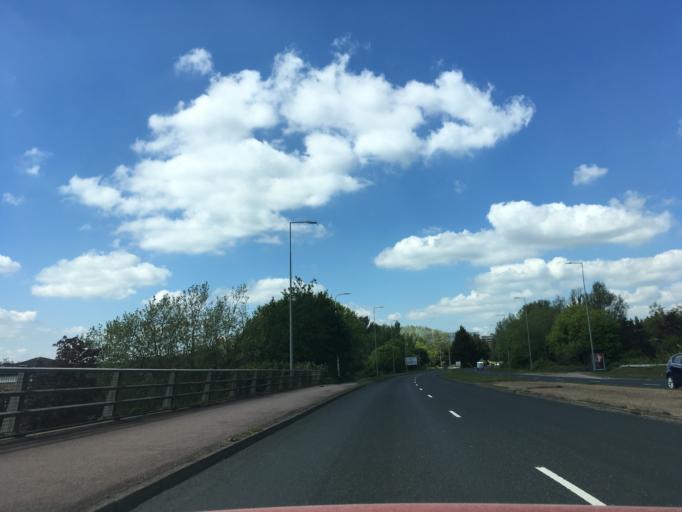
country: GB
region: England
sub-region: Milton Keynes
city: Milton Keynes
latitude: 52.0342
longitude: -0.7507
